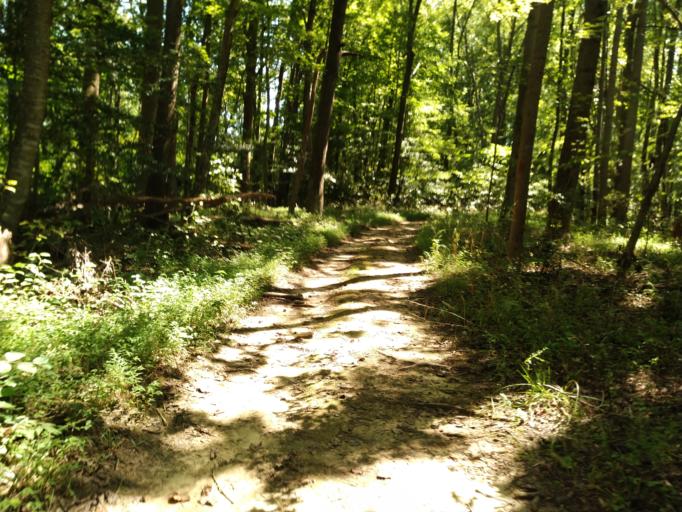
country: US
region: Maryland
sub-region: Calvert County
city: Prince Frederick
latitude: 38.5390
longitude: -76.5381
